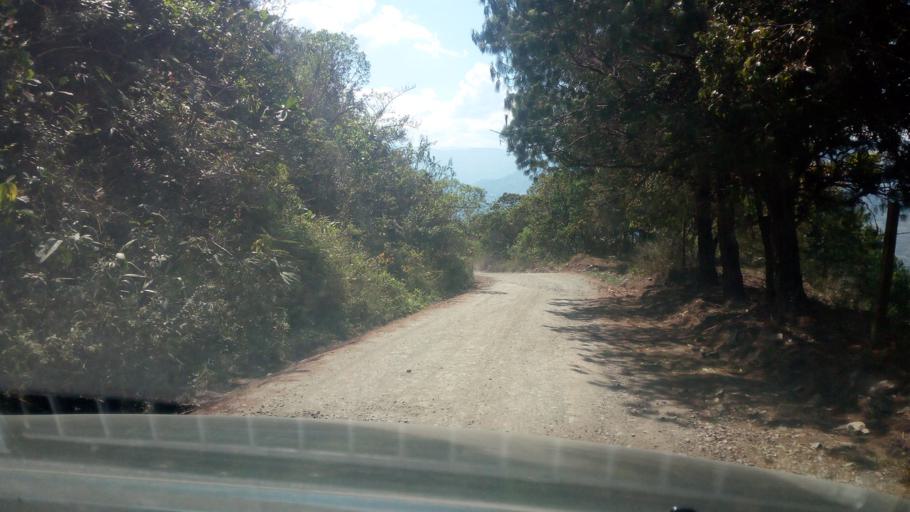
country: CO
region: Boyaca
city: Somondoco
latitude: 4.9927
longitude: -73.4114
